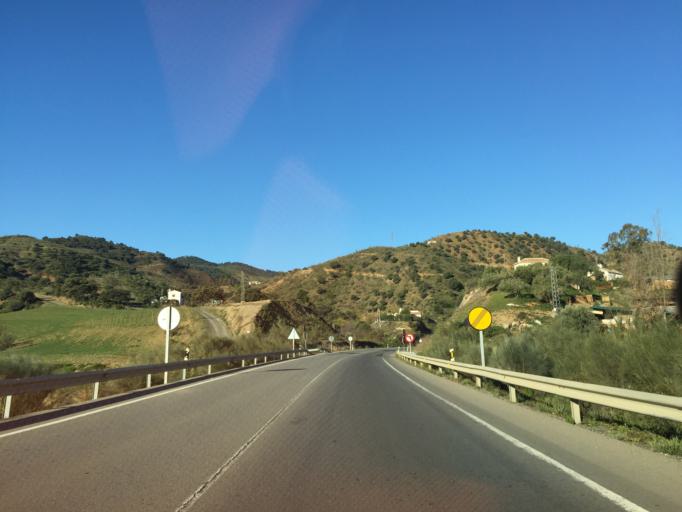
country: ES
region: Andalusia
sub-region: Provincia de Malaga
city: Alora
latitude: 36.8030
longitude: -4.7681
